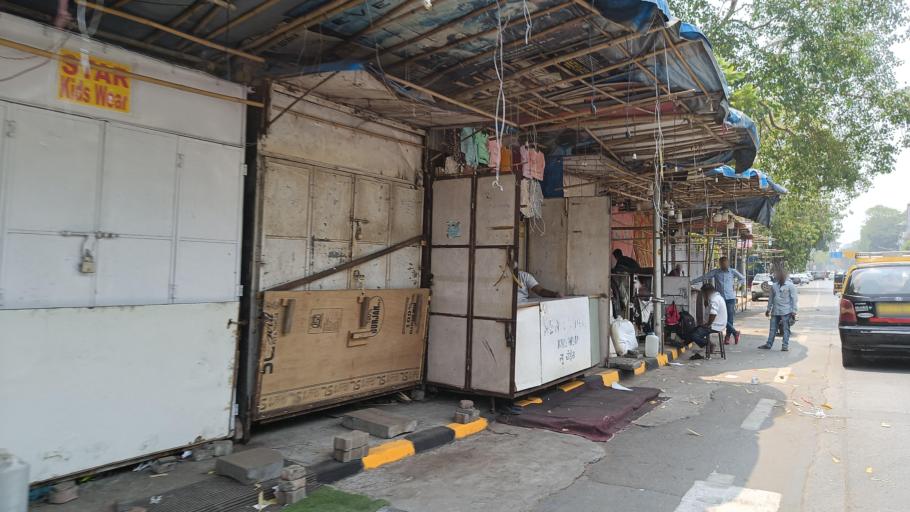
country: IN
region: Maharashtra
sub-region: Mumbai Suburban
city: Mumbai
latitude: 19.0674
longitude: 72.8337
